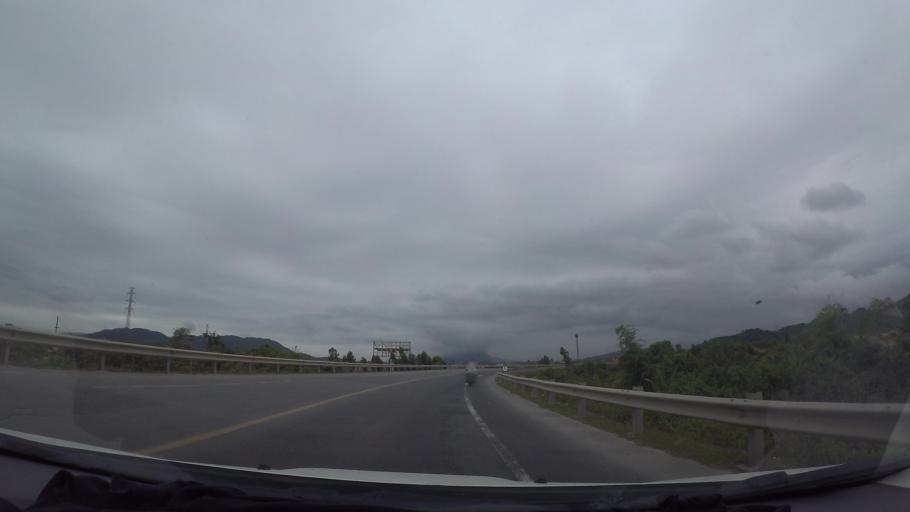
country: VN
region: Da Nang
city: Lien Chieu
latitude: 16.1091
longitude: 108.1048
